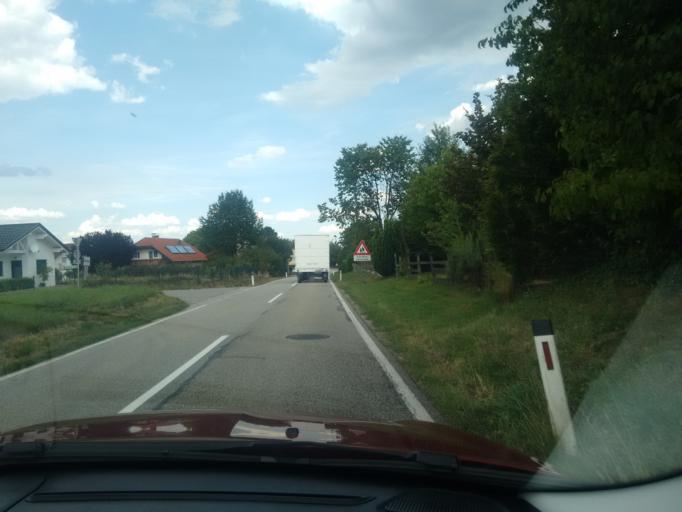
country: DE
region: Bavaria
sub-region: Upper Bavaria
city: Burghausen
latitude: 48.1647
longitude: 12.8526
